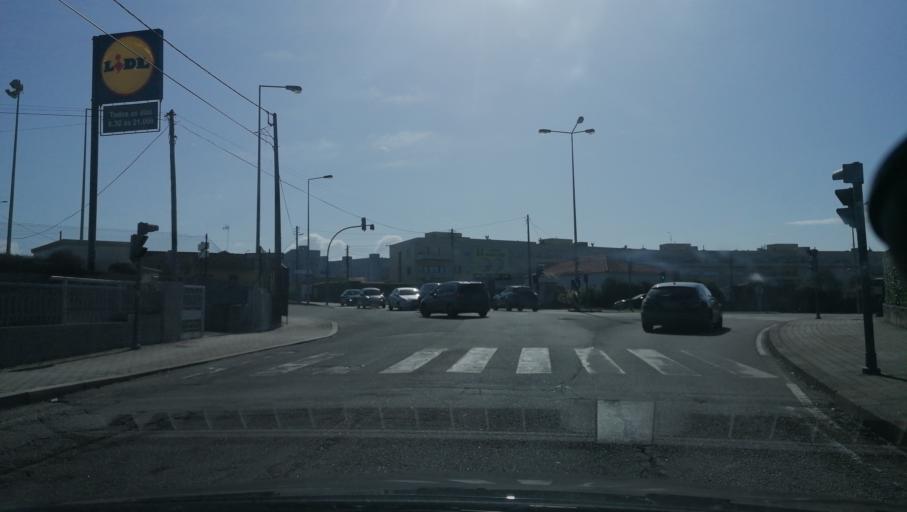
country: PT
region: Porto
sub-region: Vila Nova de Gaia
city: Sao Felix da Marinha
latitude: 41.0300
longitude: -8.6418
